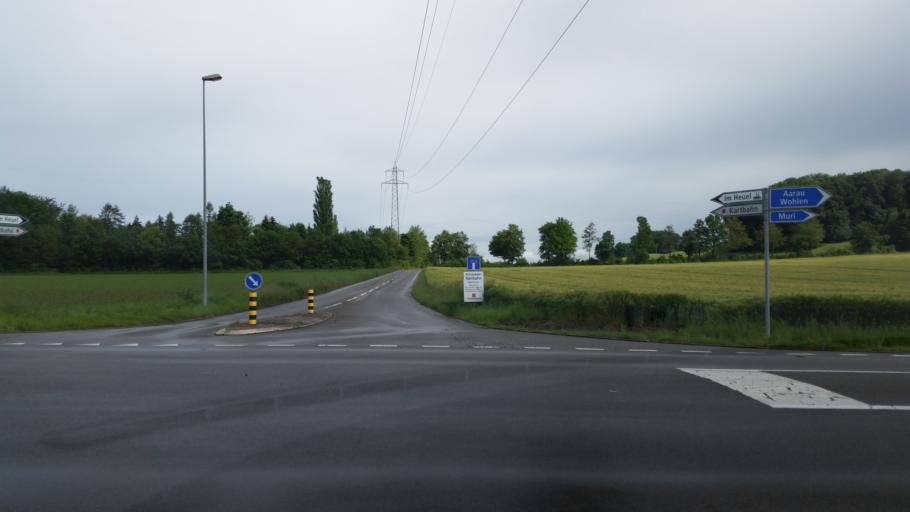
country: CH
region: Aargau
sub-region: Bezirk Muri
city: Waltenschwil
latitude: 47.3287
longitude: 8.2913
